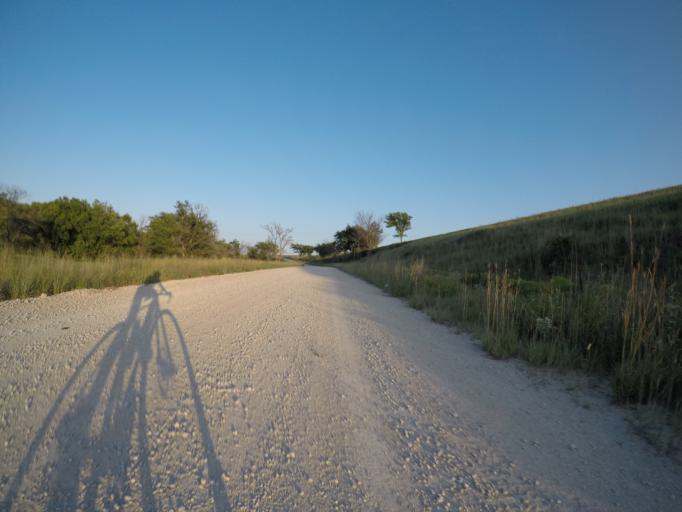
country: US
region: Kansas
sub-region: Riley County
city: Ogden
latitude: 39.0095
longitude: -96.6422
